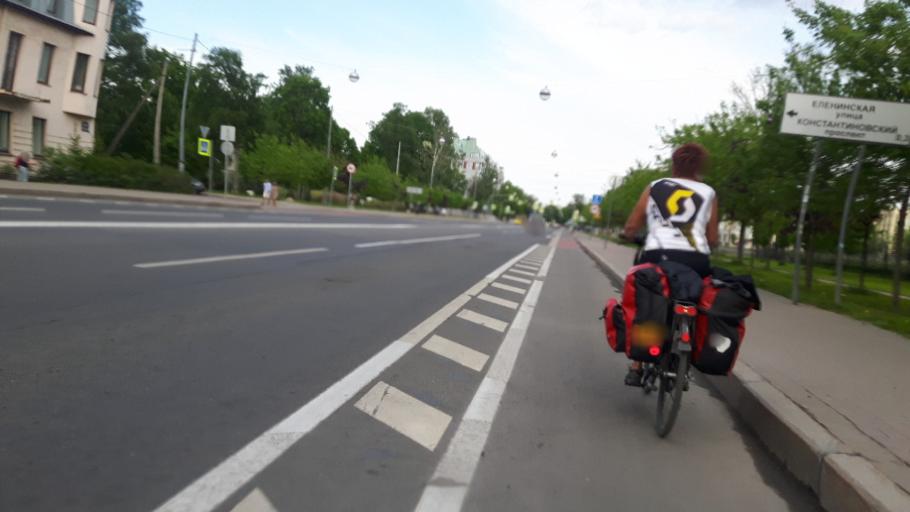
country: RU
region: Leningrad
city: Krestovskiy ostrov
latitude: 59.9710
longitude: 30.2646
